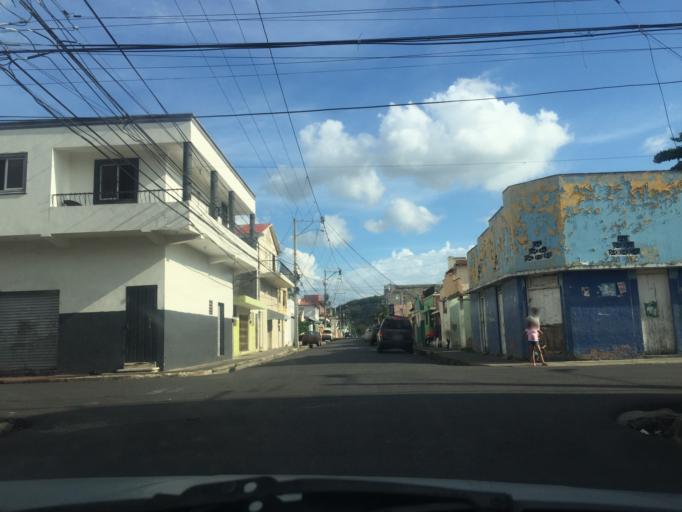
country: DO
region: Santiago
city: Santiago de los Caballeros
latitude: 19.4551
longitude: -70.7125
